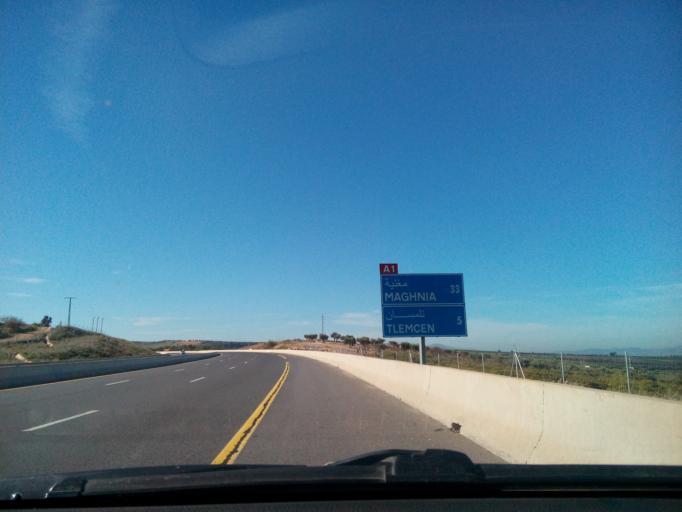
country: DZ
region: Tlemcen
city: Chetouane
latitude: 34.9421
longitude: -1.3259
